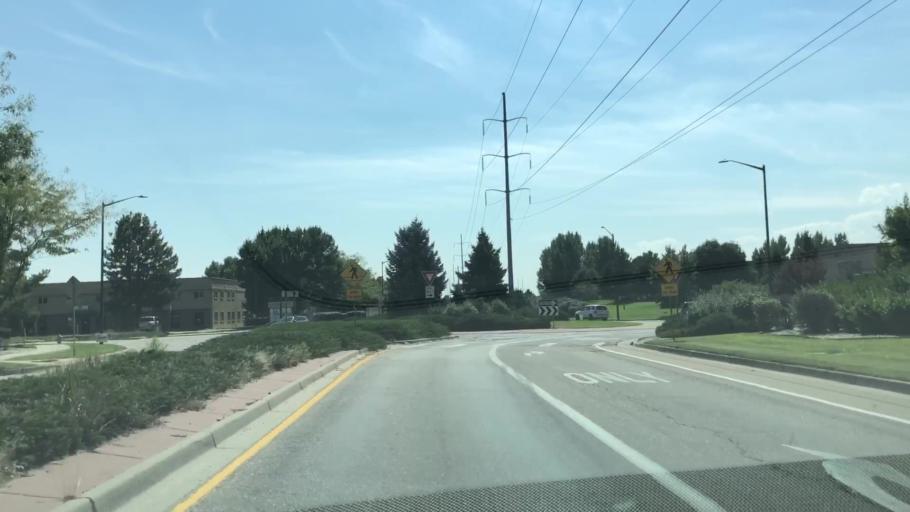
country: US
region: Colorado
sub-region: Larimer County
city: Loveland
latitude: 40.4059
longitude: -105.0447
